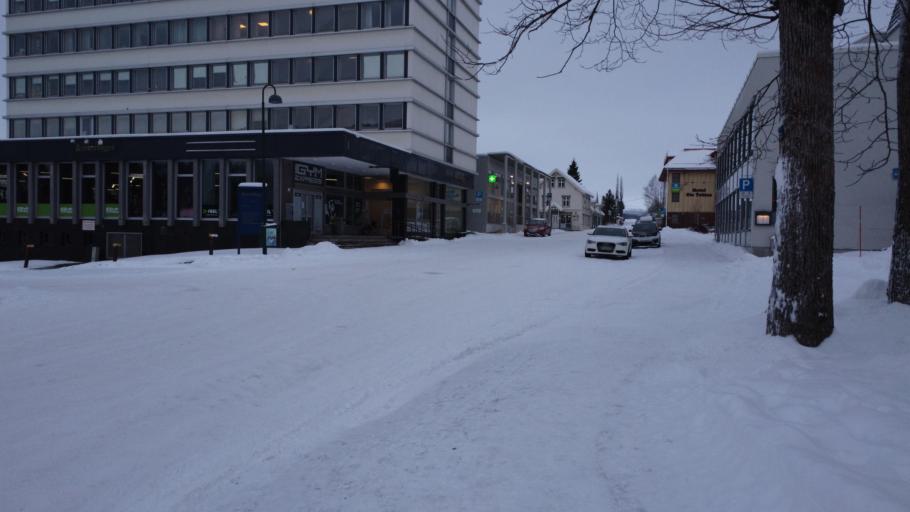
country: NO
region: Nordland
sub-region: Rana
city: Mo i Rana
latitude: 66.3119
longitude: 14.1342
